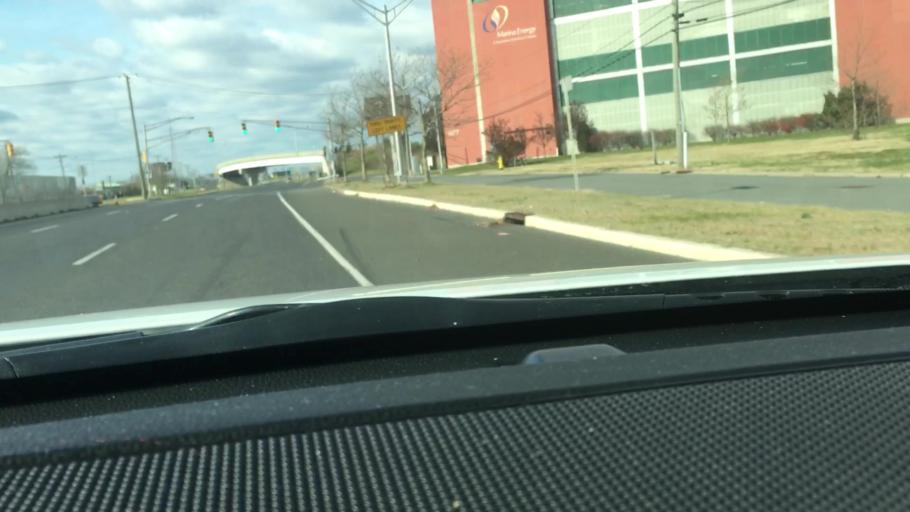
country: US
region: New Jersey
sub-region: Atlantic County
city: Atlantic City
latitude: 39.3724
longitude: -74.4357
